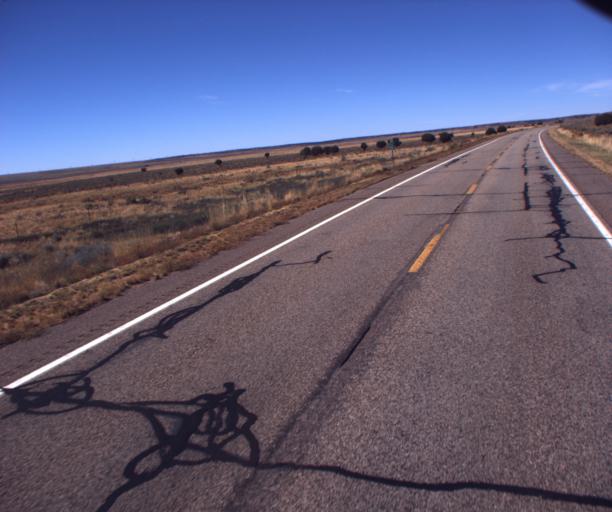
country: US
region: Arizona
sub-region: Mohave County
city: Colorado City
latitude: 36.8590
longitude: -112.8104
